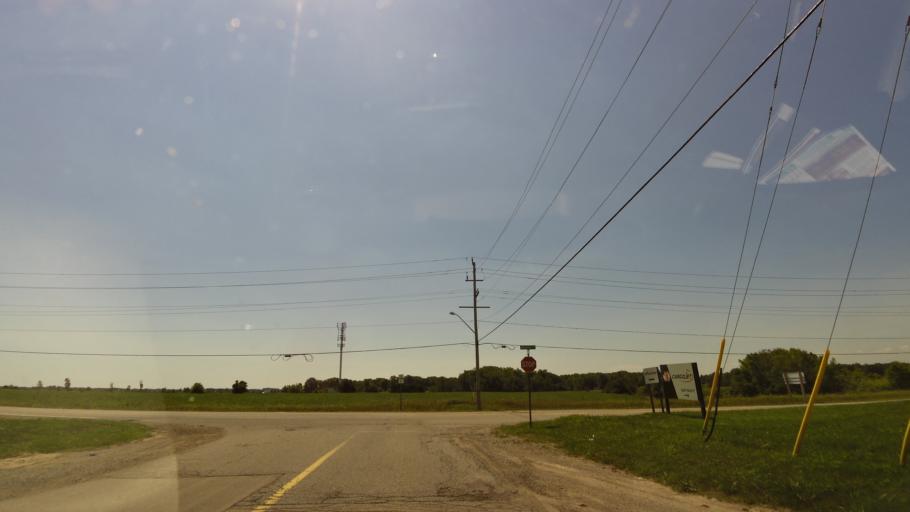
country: CA
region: Ontario
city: Ancaster
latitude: 43.1603
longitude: -79.9300
